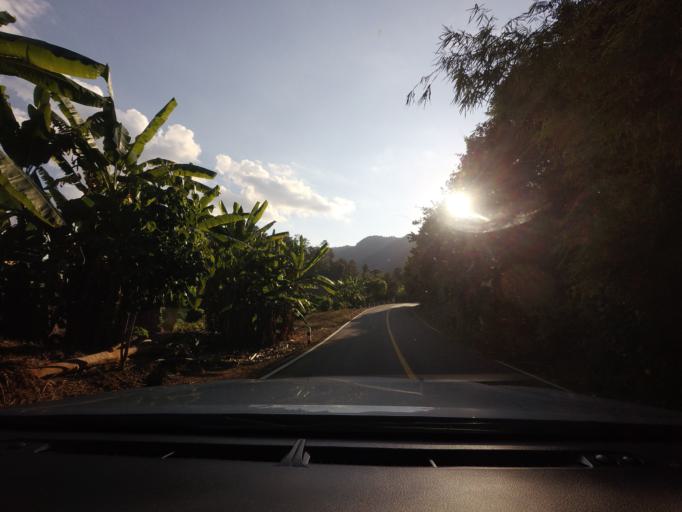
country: TH
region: Chiang Mai
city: Chai Prakan
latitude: 19.5546
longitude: 99.1656
